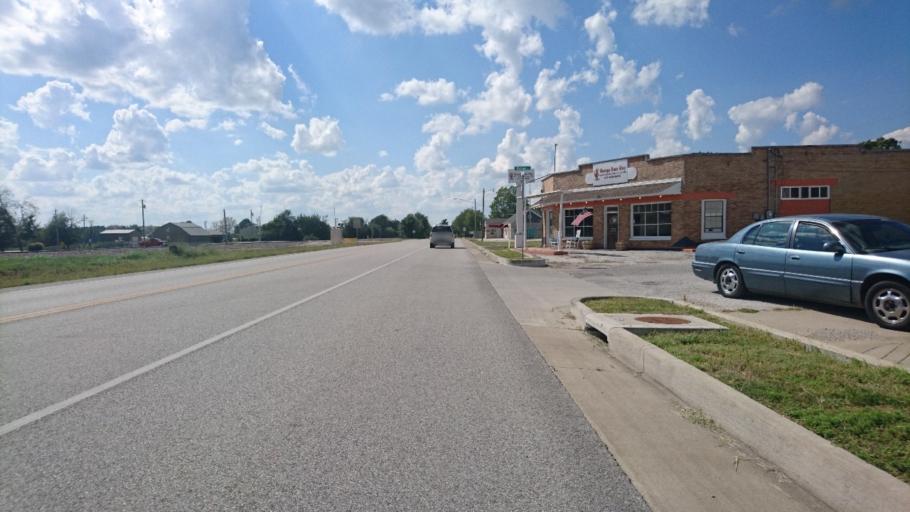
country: US
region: Missouri
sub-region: Greene County
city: Strafford
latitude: 37.2686
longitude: -93.1170
